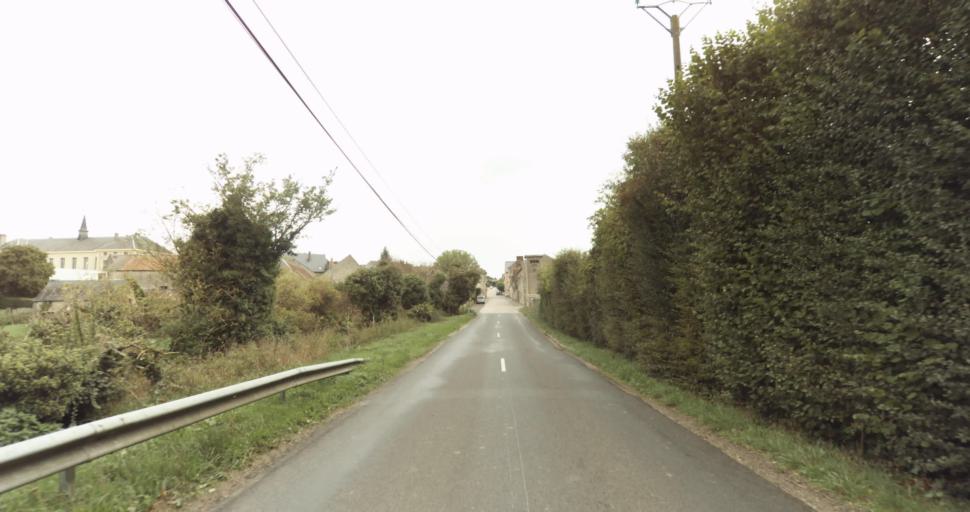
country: FR
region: Lower Normandy
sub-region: Departement de l'Orne
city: Gace
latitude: 48.6990
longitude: 0.2856
